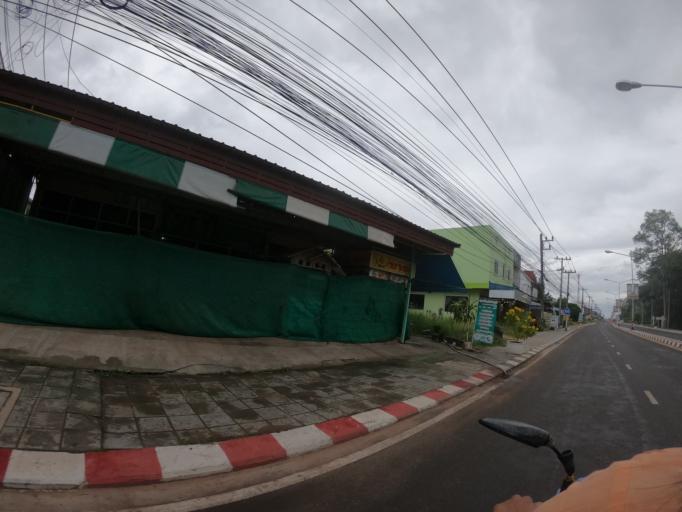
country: TH
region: Roi Et
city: Chiang Khwan
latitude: 16.1469
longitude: 103.8687
